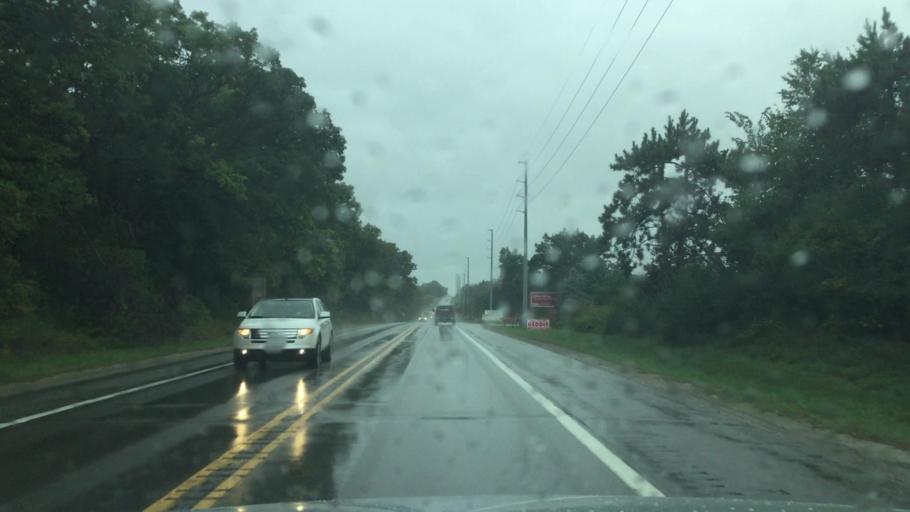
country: US
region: Michigan
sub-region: Livingston County
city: Howell
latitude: 42.6300
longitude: -83.8650
